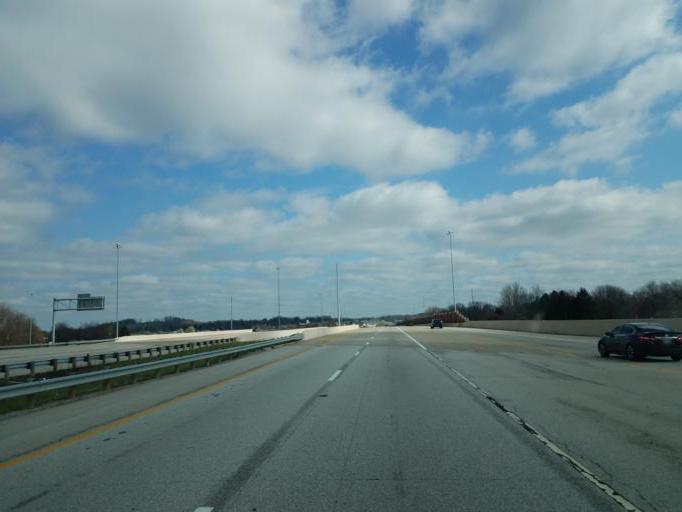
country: US
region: Ohio
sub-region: Summit County
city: Macedonia
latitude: 41.3027
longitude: -81.5183
